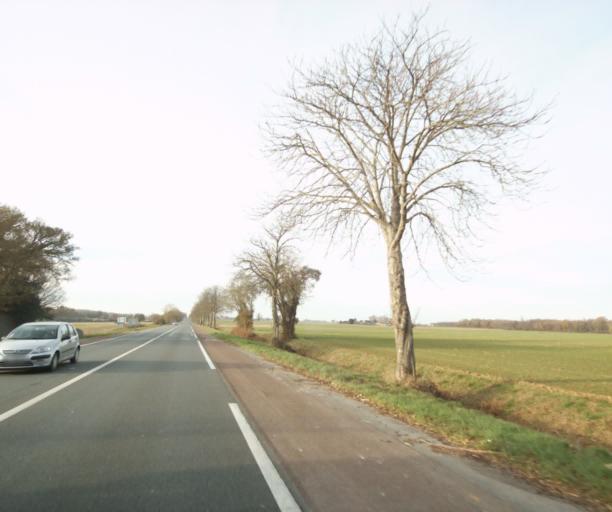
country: FR
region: Poitou-Charentes
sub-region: Departement de la Charente-Maritime
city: Saint-Georges-des-Coteaux
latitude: 45.7936
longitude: -0.7312
